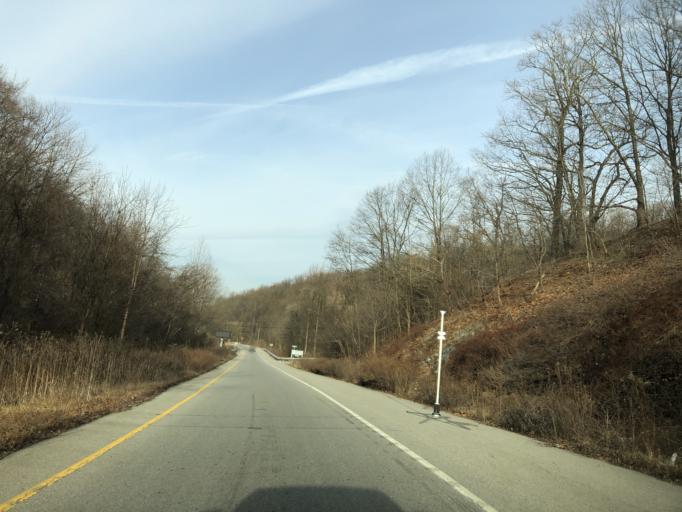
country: US
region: Pennsylvania
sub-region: Chester County
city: Exton
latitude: 40.0135
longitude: -75.6156
